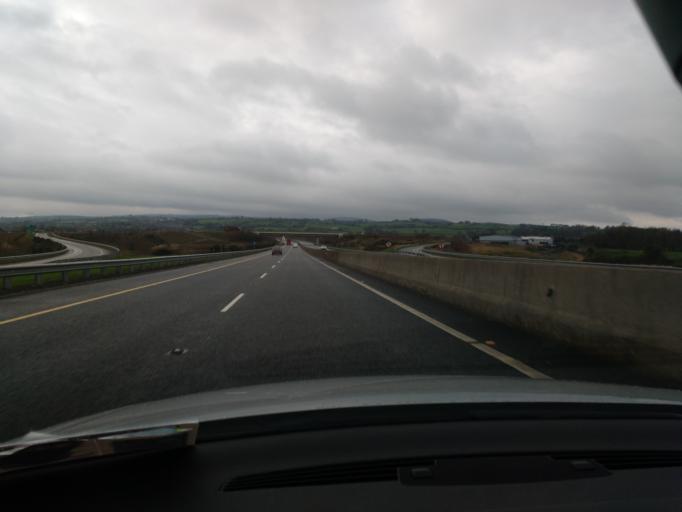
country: IE
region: Munster
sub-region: North Tipperary
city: Nenagh
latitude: 52.8450
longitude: -8.2432
